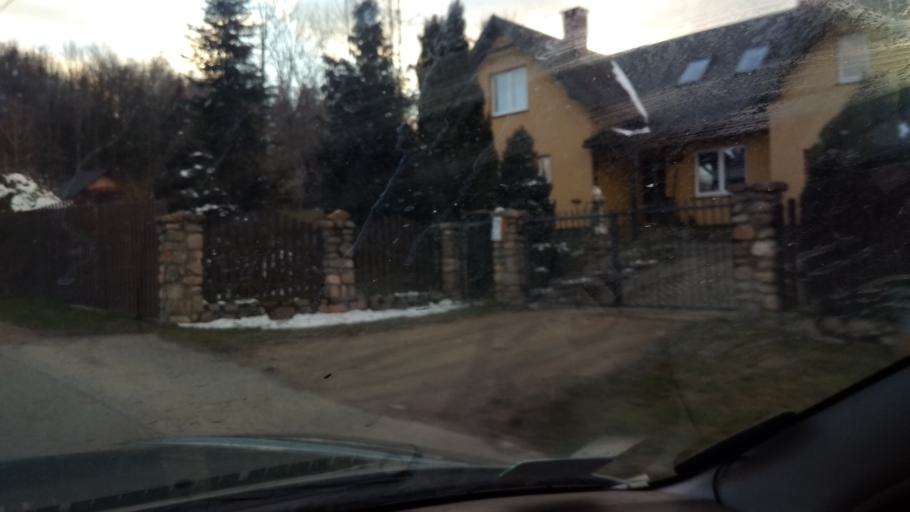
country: PL
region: Lower Silesian Voivodeship
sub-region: Powiat jeleniogorski
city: Sosnowka
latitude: 50.8418
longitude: 15.7386
